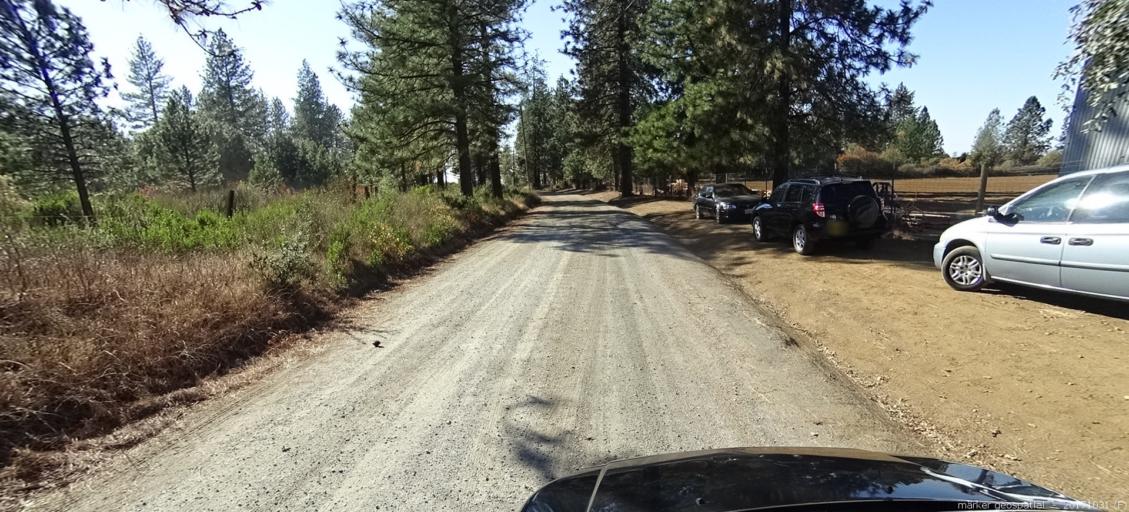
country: US
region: California
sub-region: Shasta County
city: Shingletown
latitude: 40.4644
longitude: -121.9981
